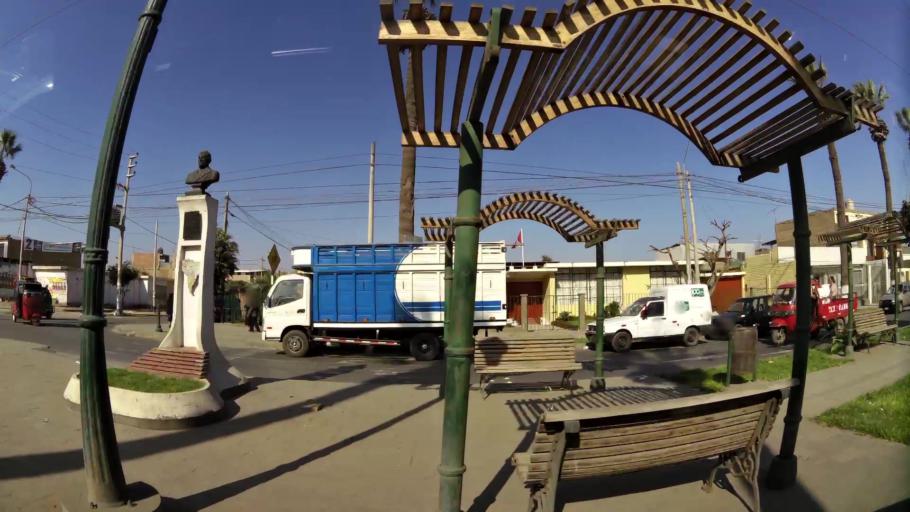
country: PE
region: Ica
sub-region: Provincia de Chincha
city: Chincha Alta
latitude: -13.4116
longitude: -76.1316
